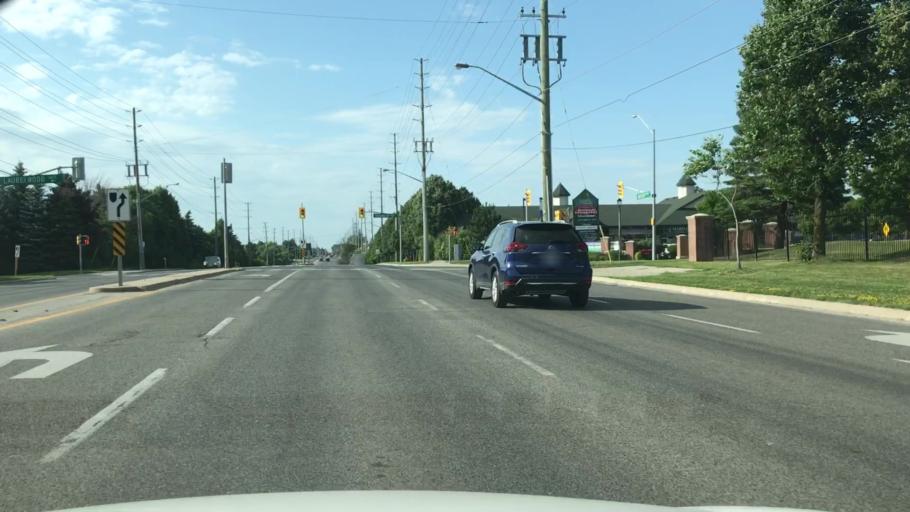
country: CA
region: Ontario
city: Newmarket
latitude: 44.0288
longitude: -79.4491
